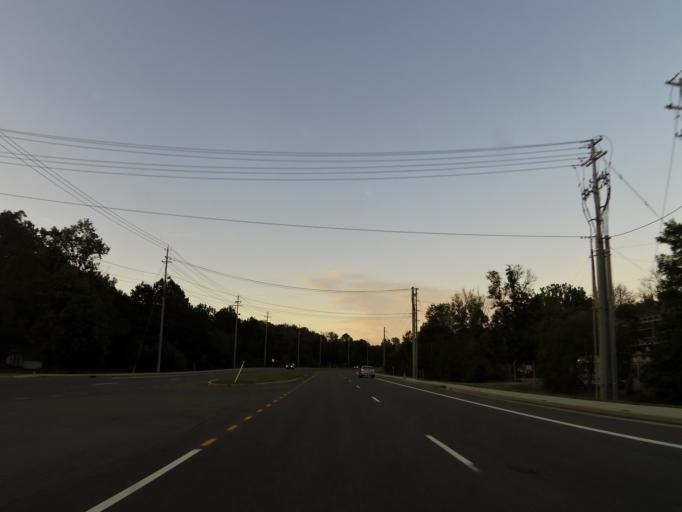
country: US
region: Tennessee
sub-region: Anderson County
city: Oak Ridge
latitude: 35.9972
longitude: -84.3052
